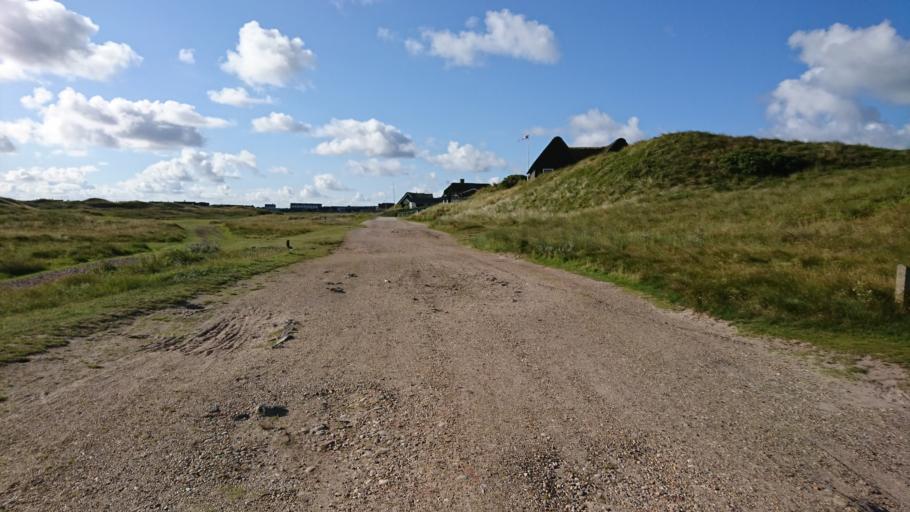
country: DK
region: South Denmark
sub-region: Fano Kommune
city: Nordby
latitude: 55.4420
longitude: 8.3618
